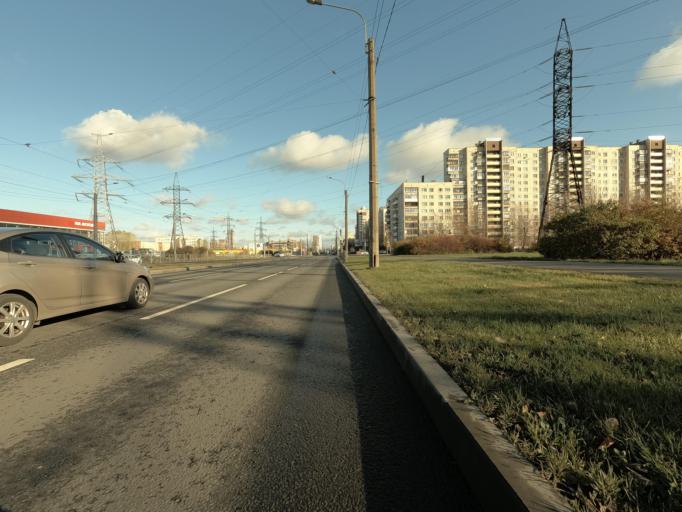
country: RU
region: St.-Petersburg
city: Krasnogvargeisky
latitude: 59.9536
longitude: 30.4588
